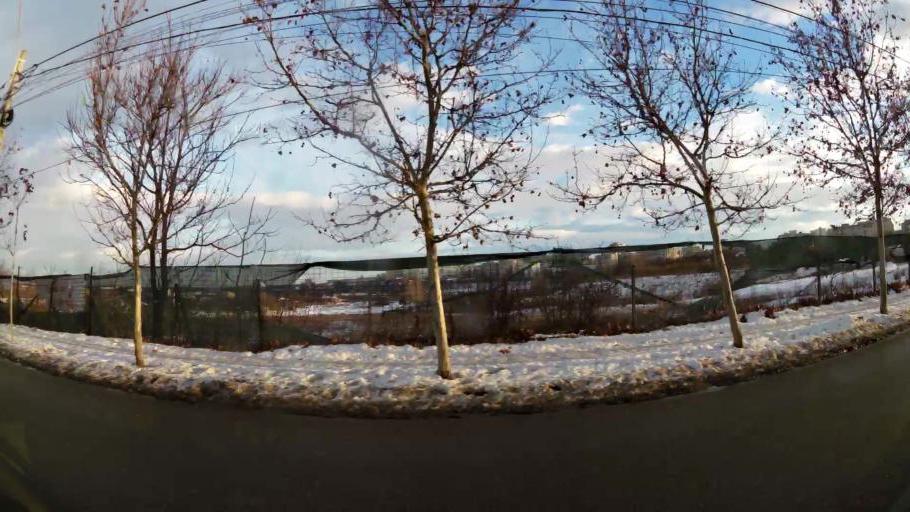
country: RO
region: Ilfov
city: Dobroesti
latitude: 44.4474
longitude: 26.1720
